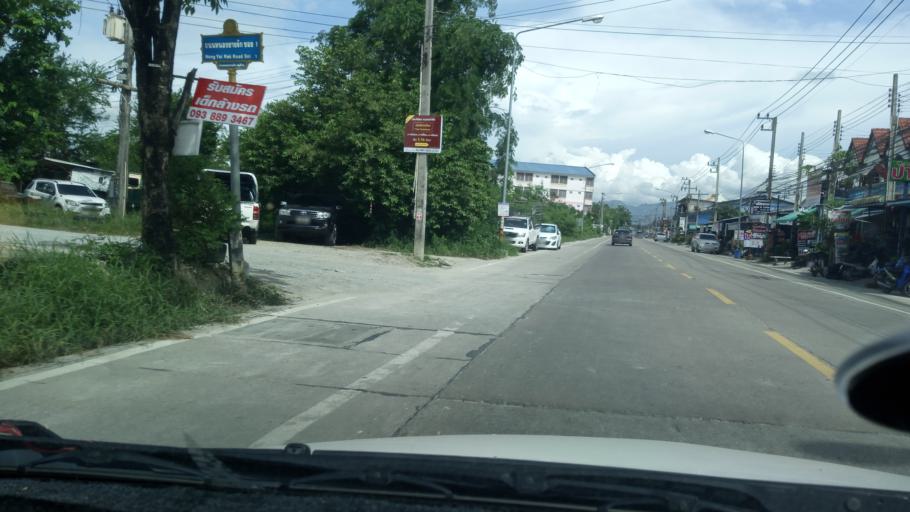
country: TH
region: Chon Buri
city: Chon Buri
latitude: 13.4049
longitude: 101.0293
